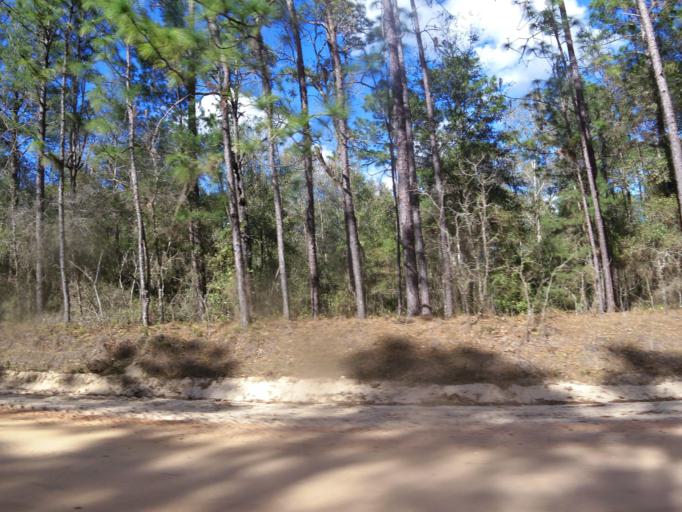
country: US
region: Florida
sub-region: Putnam County
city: Interlachen
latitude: 29.7839
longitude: -81.8644
